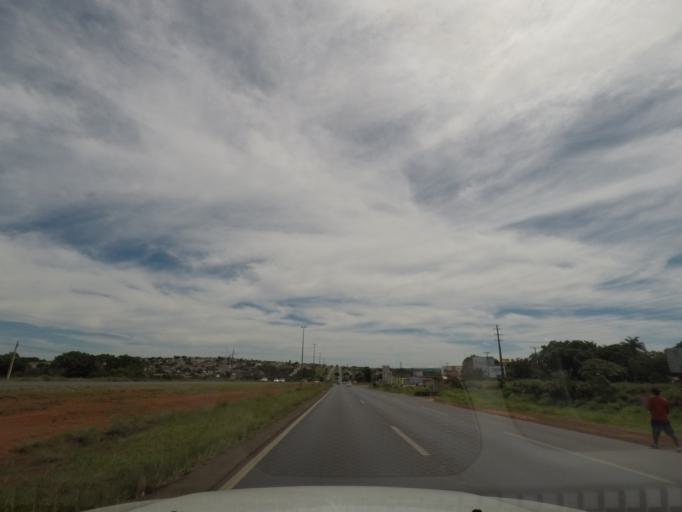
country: BR
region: Goias
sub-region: Planaltina
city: Planaltina
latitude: -15.6105
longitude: -47.6972
